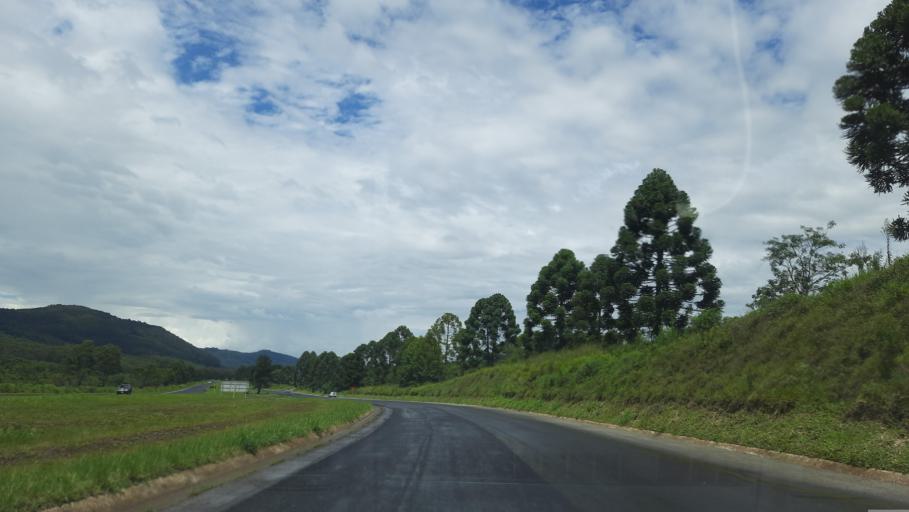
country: BR
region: Minas Gerais
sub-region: Pocos De Caldas
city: Pocos de Caldas
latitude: -21.8213
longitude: -46.6653
